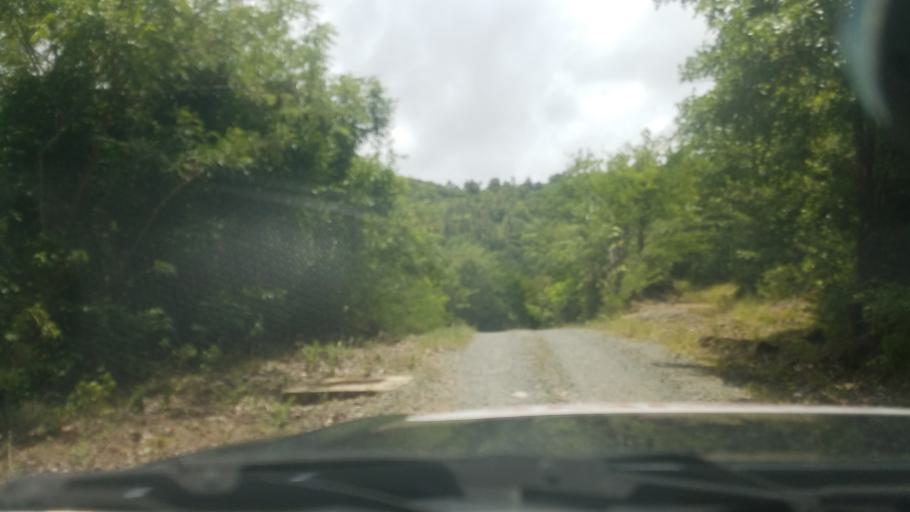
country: LC
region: Praslin
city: Praslin
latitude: 13.8669
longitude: -60.9064
